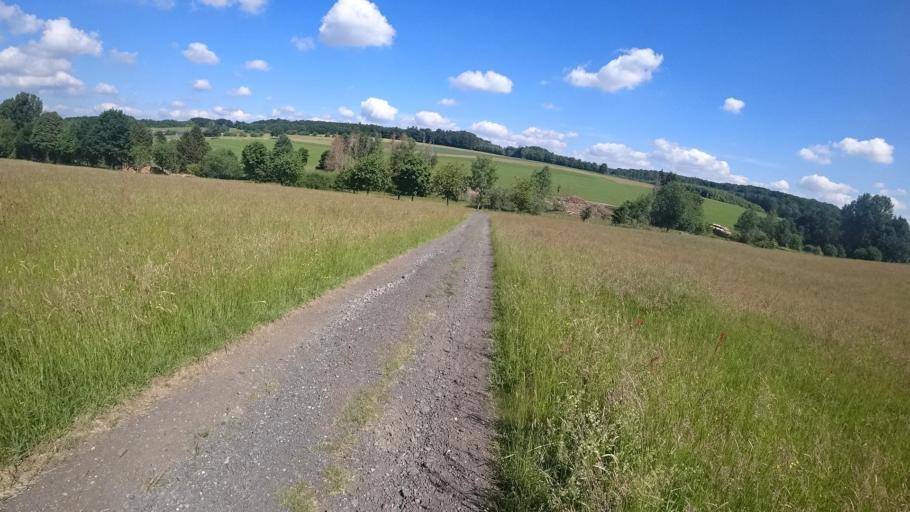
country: DE
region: Rheinland-Pfalz
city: Sorth
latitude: 50.6959
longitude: 7.6936
